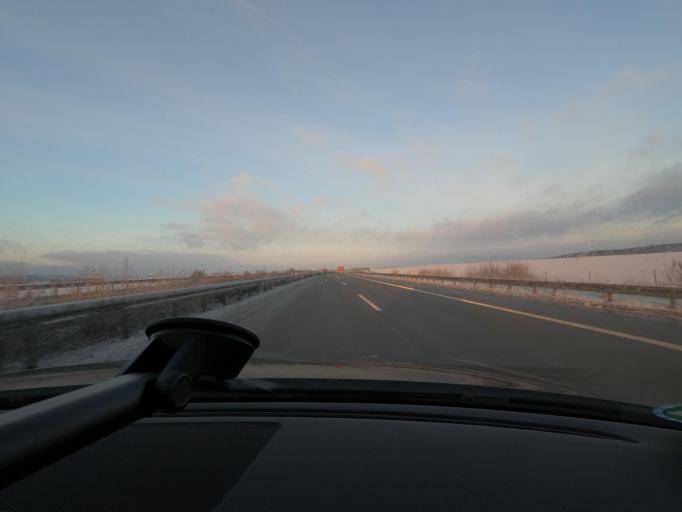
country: DE
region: Thuringia
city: Wingerode
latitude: 51.3946
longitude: 10.2719
